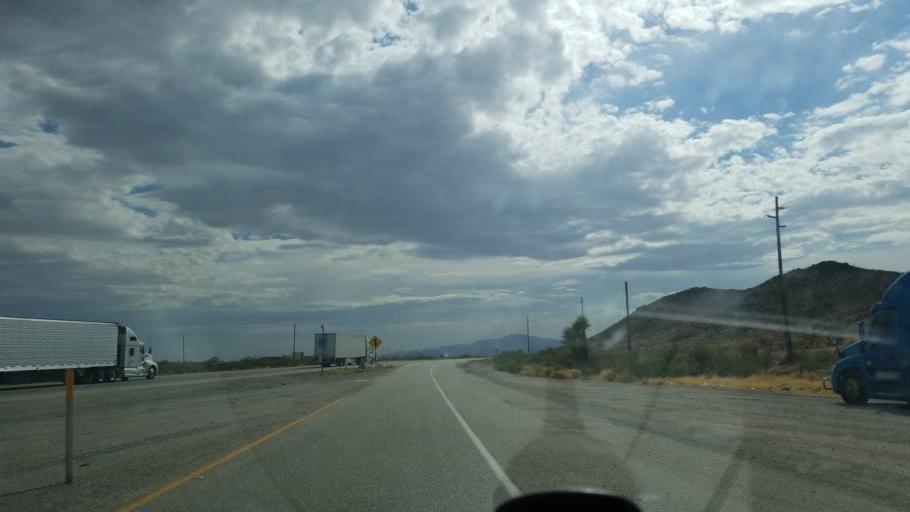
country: US
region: California
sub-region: San Bernardino County
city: Needles
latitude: 34.8302
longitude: -115.0537
